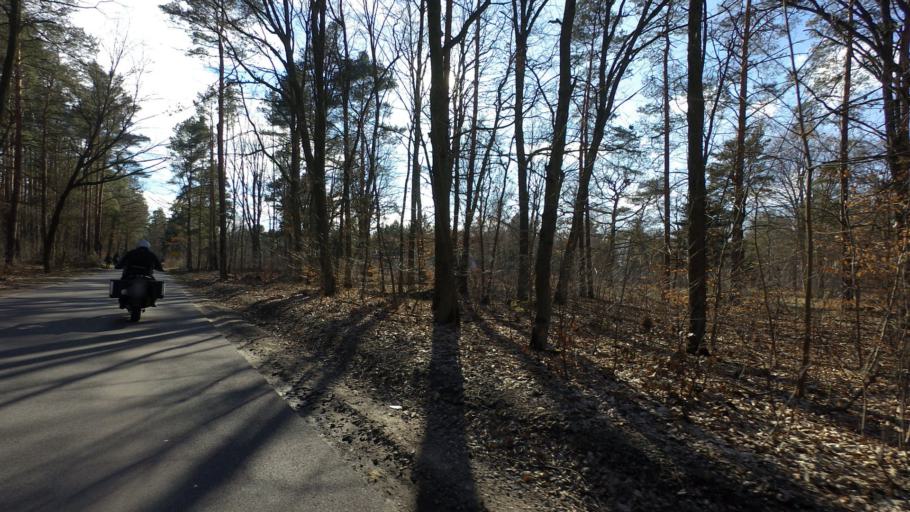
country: DE
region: Brandenburg
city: Oranienburg
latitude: 52.7572
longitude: 13.2794
